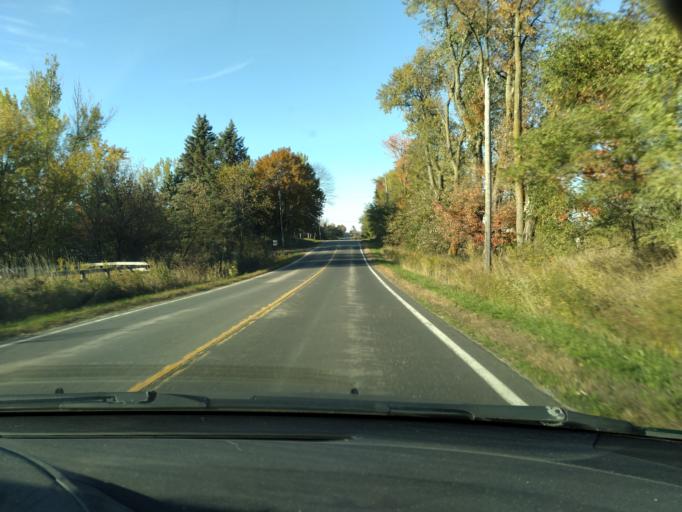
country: CA
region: Ontario
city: Bradford West Gwillimbury
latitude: 43.9218
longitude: -79.7084
